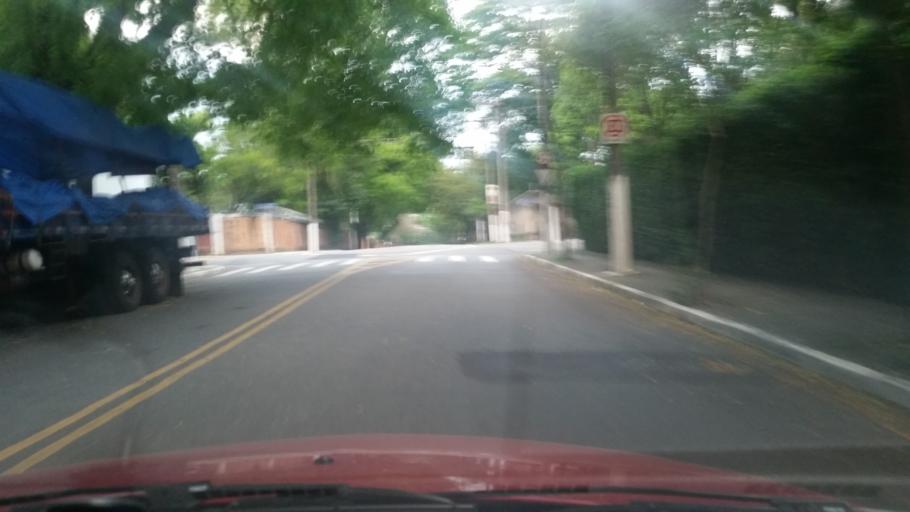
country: BR
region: Sao Paulo
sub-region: Diadema
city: Diadema
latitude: -23.6370
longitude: -46.6918
